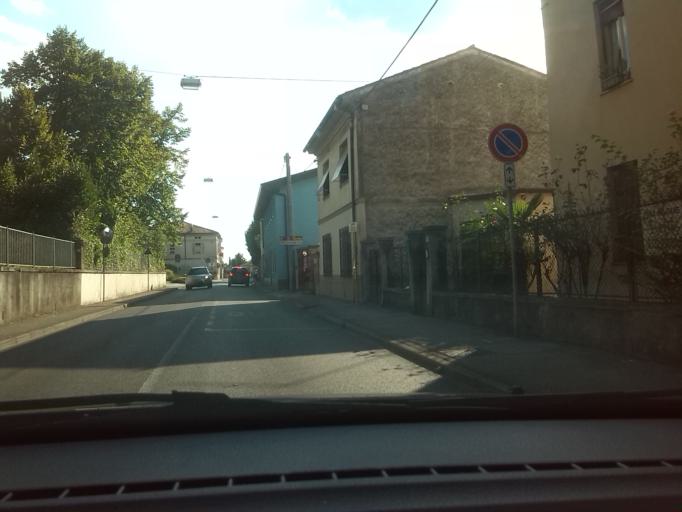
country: IT
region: Friuli Venezia Giulia
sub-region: Provincia di Gorizia
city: Gorizia
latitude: 45.9234
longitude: 13.6028
